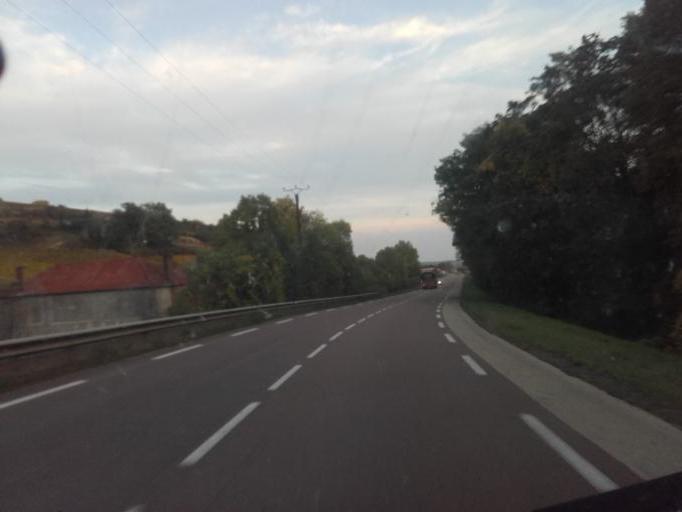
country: FR
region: Bourgogne
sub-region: Departement de la Cote-d'Or
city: Corpeau
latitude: 46.9526
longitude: 4.7235
